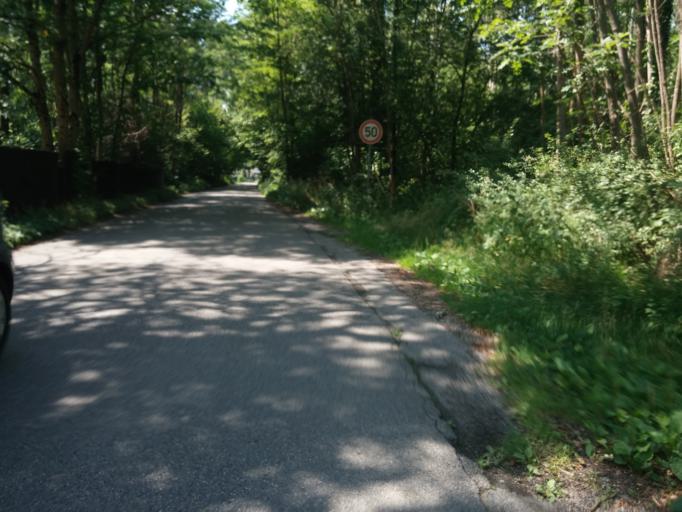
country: DE
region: Bavaria
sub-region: Upper Bavaria
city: Neubiberg
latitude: 48.1070
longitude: 11.6788
